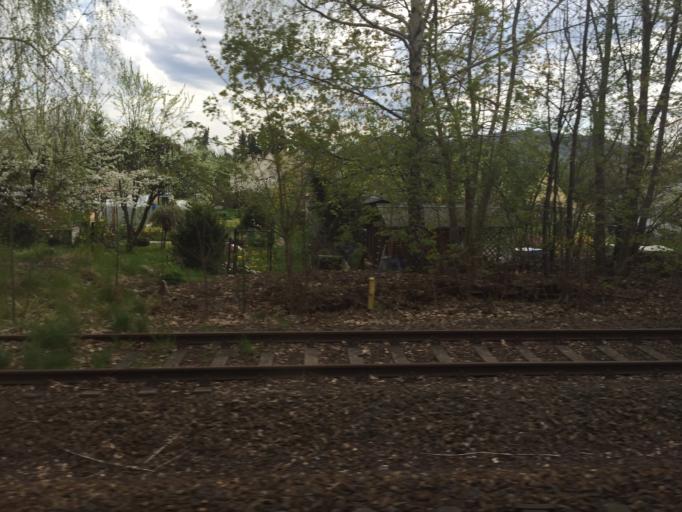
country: DE
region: Saxony
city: Lobau
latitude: 51.1055
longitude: 14.6623
